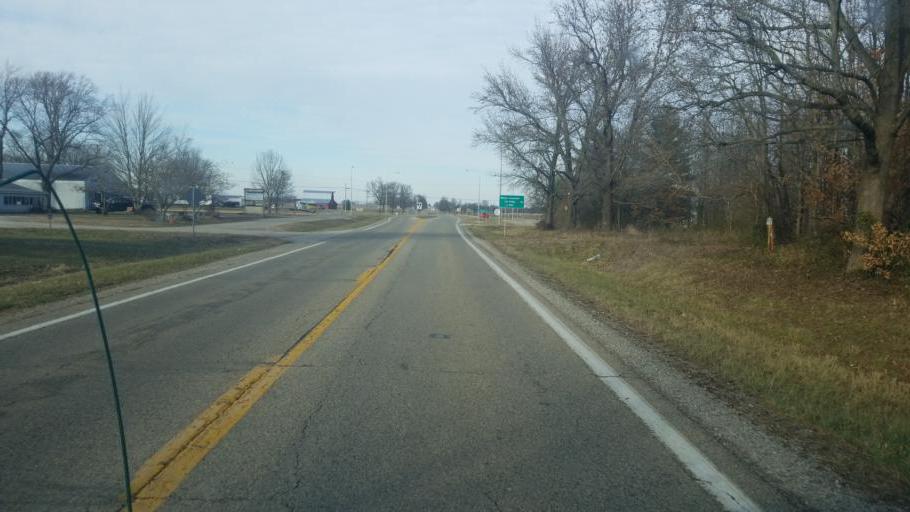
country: US
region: Illinois
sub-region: Lawrence County
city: Bridgeport
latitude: 38.5883
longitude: -87.6944
